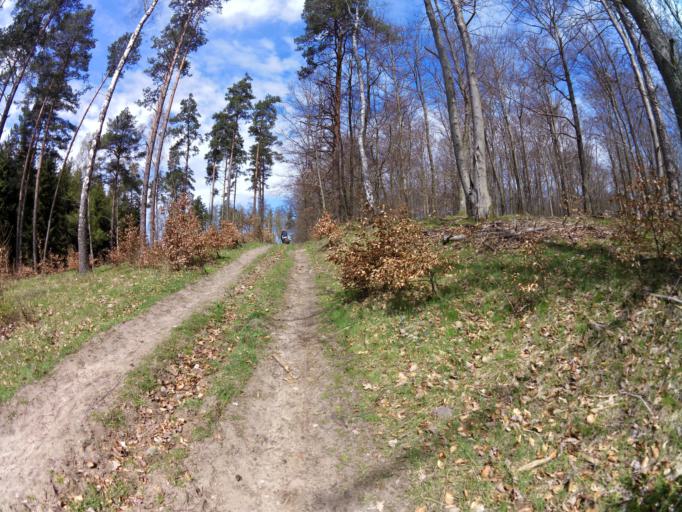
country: PL
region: West Pomeranian Voivodeship
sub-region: Powiat szczecinecki
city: Szczecinek
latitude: 53.7810
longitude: 16.6188
